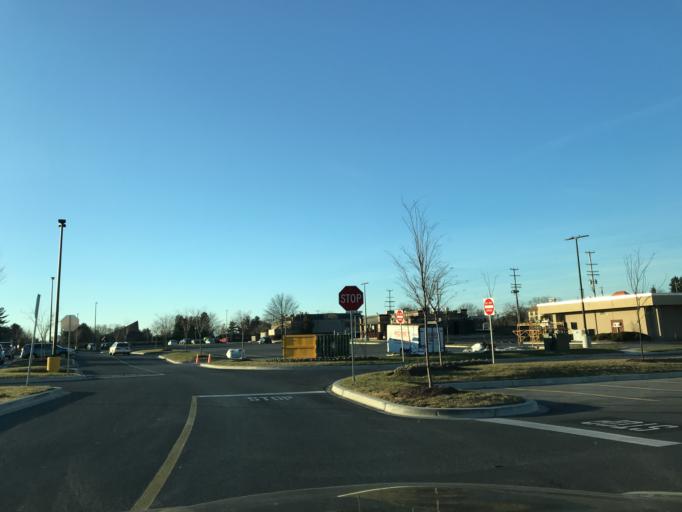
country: US
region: Maryland
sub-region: Carroll County
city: Eldersburg
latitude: 39.3981
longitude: -76.9335
